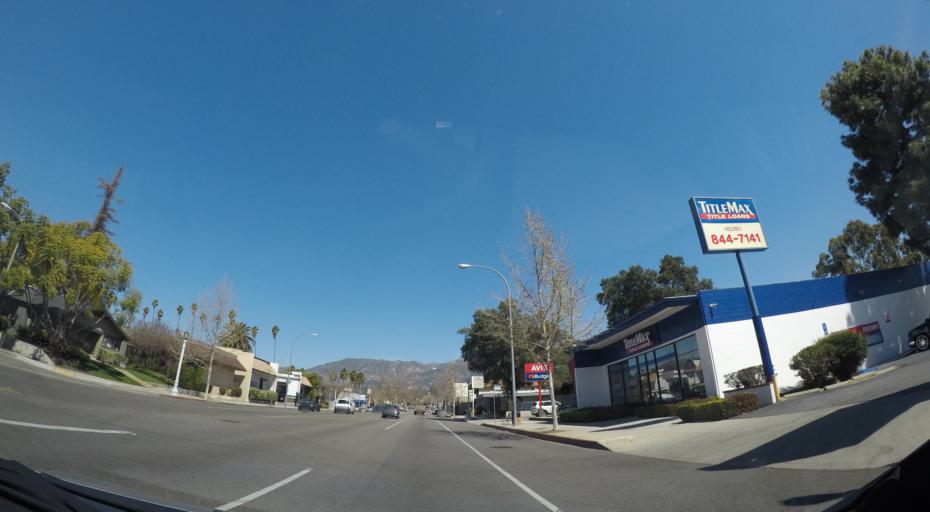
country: US
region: California
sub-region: Los Angeles County
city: Pasadena
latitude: 34.1555
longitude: -118.1324
